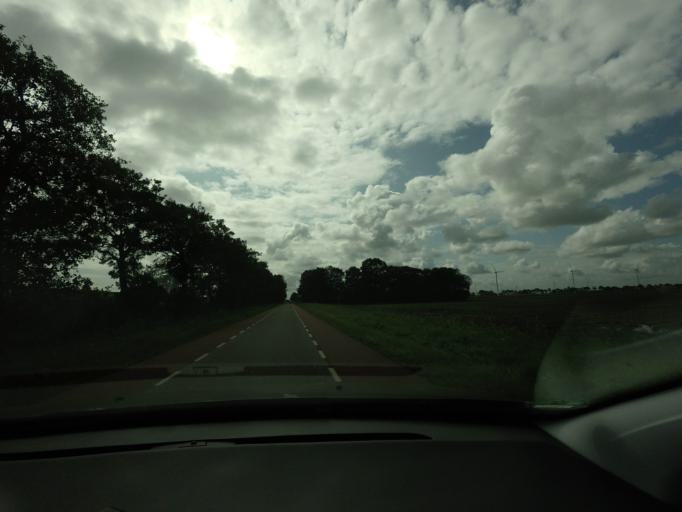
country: NL
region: North Holland
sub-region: Gemeente Medemblik
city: Medemblik
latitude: 52.8414
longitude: 5.1120
